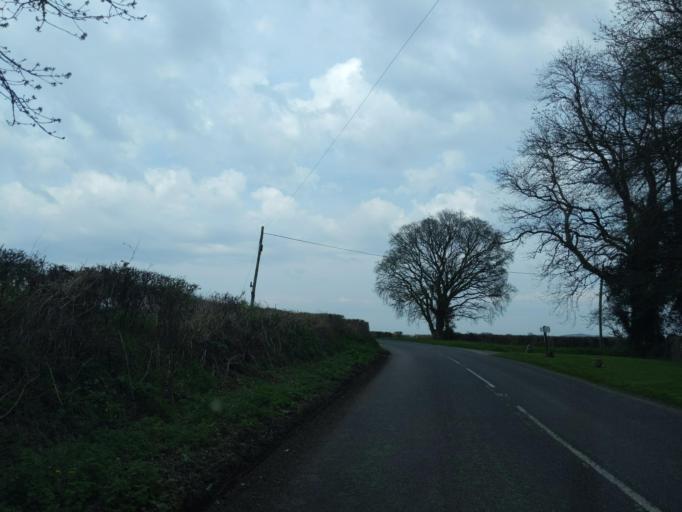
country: GB
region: England
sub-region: Devon
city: Bovey Tracey
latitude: 50.6518
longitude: -3.8031
